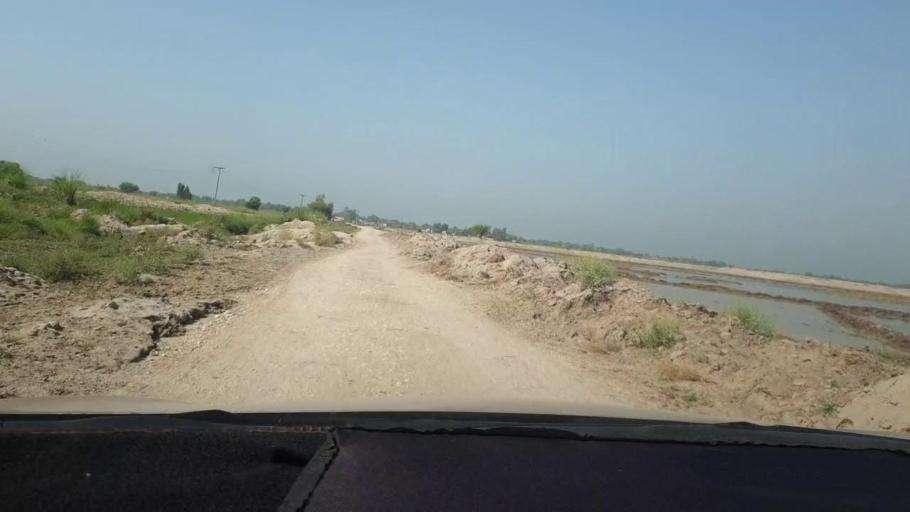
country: PK
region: Sindh
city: Miro Khan
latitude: 27.7120
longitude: 68.1025
